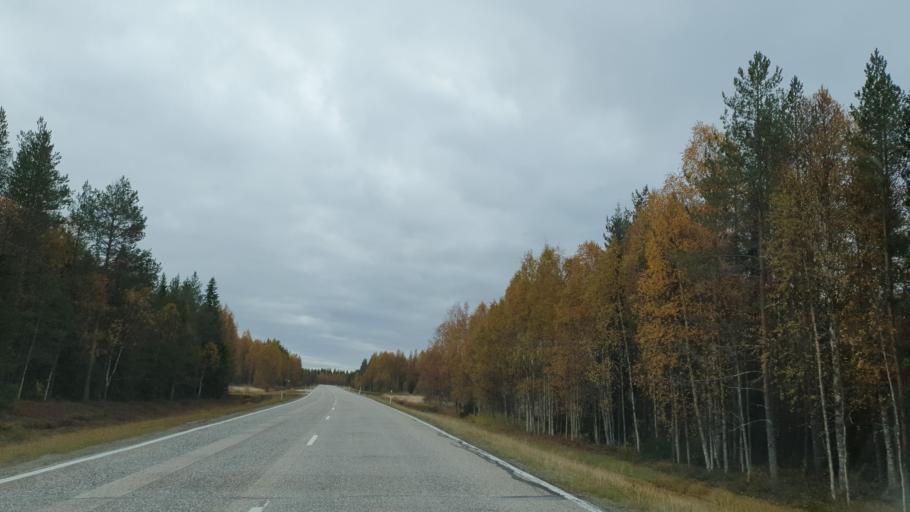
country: FI
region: Lapland
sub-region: Rovaniemi
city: Ranua
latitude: 65.6712
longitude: 26.6868
